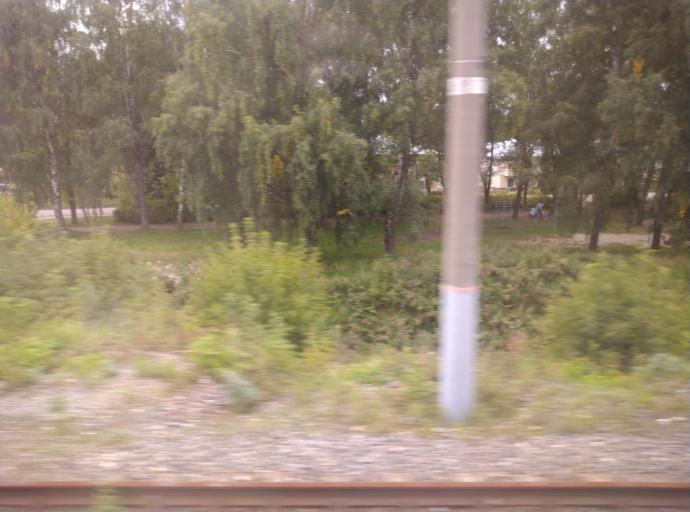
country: RU
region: Kostroma
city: Nerekhta
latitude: 57.4646
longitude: 40.5552
